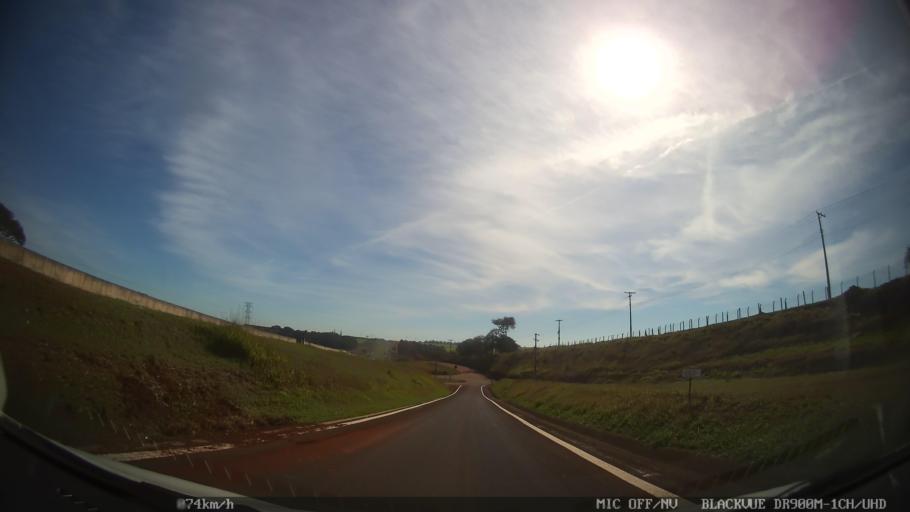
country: BR
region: Sao Paulo
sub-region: Araras
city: Araras
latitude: -22.3138
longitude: -47.3905
